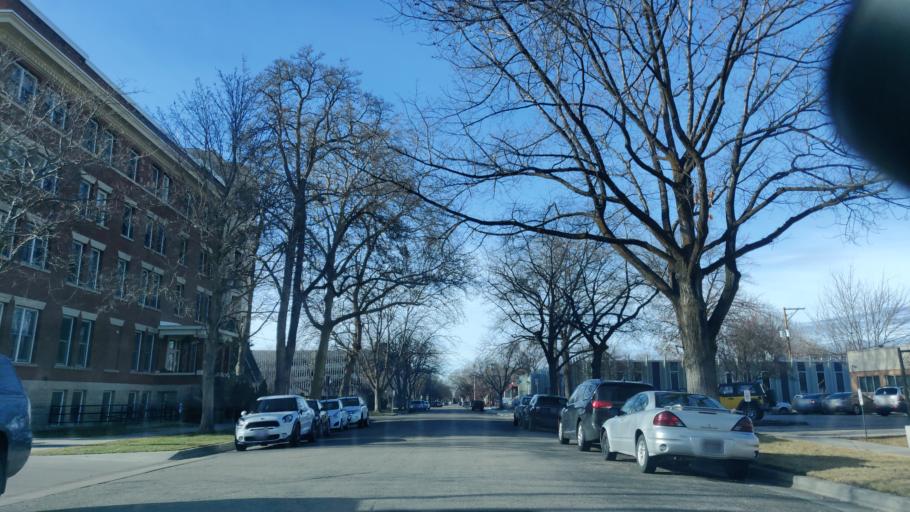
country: US
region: Idaho
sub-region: Ada County
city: Boise
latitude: 43.6167
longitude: -116.1945
